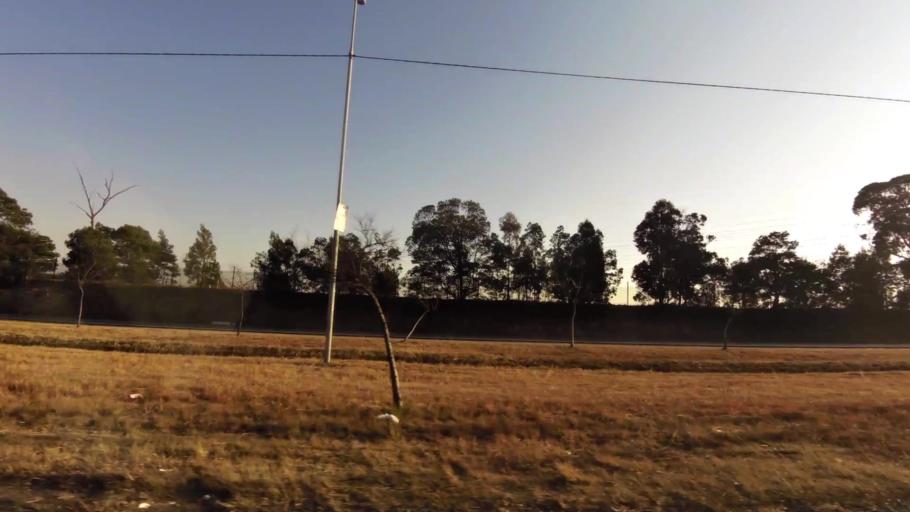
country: ZA
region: Gauteng
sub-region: City of Johannesburg Metropolitan Municipality
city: Johannesburg
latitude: -26.2675
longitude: 27.9714
